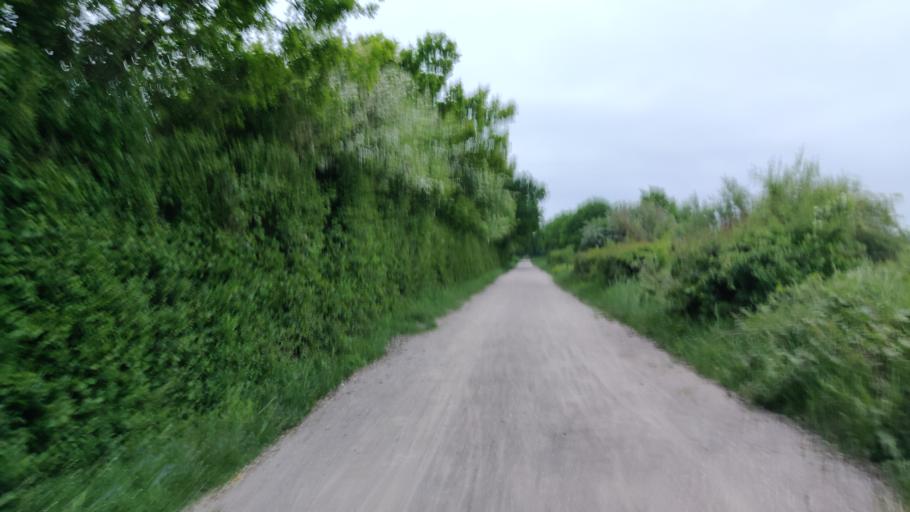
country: GB
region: England
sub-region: West Sussex
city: Partridge Green
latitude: 50.9807
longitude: -0.3154
